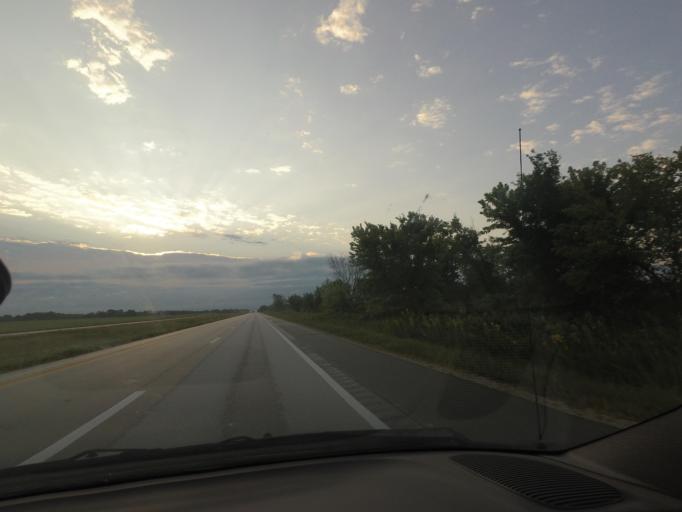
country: US
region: Missouri
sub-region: Shelby County
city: Shelbina
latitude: 39.7263
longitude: -92.1797
